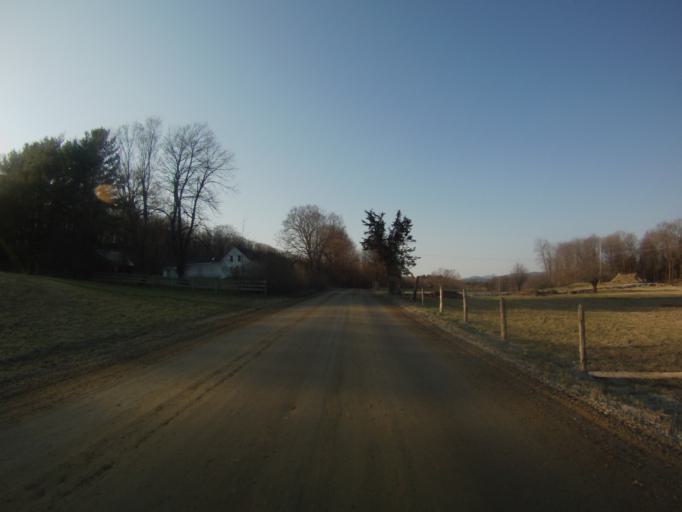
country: US
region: Vermont
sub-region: Addison County
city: Middlebury (village)
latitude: 44.0377
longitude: -73.1460
